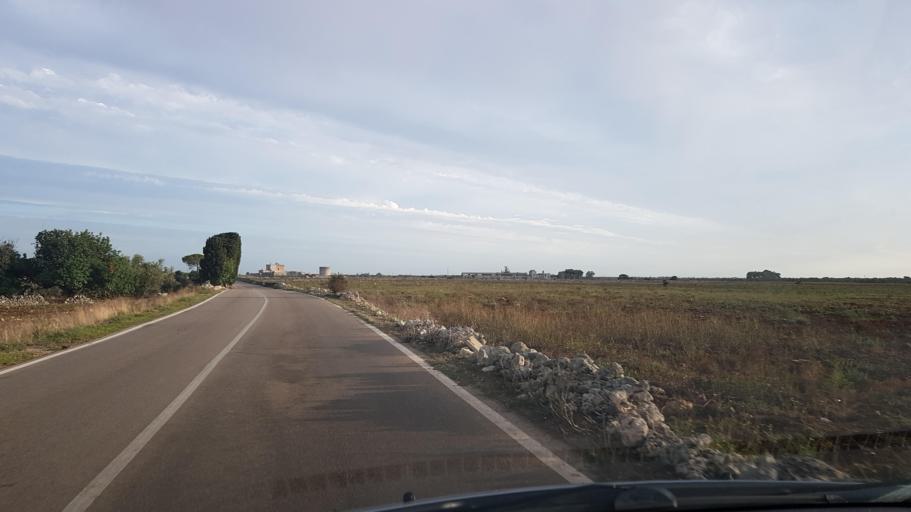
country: IT
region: Apulia
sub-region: Provincia di Lecce
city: Trepuzzi
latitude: 40.4428
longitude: 18.1098
